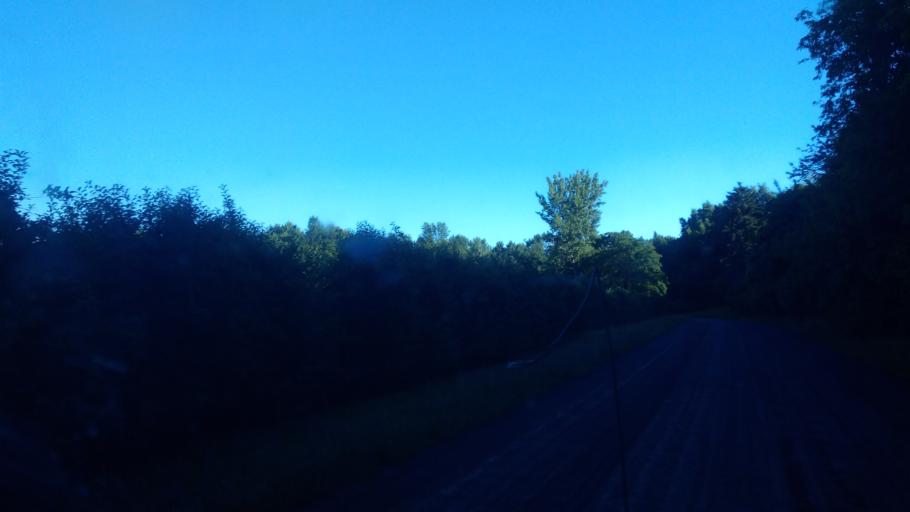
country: US
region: New York
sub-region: Wayne County
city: Sodus
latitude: 43.1682
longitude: -77.0593
